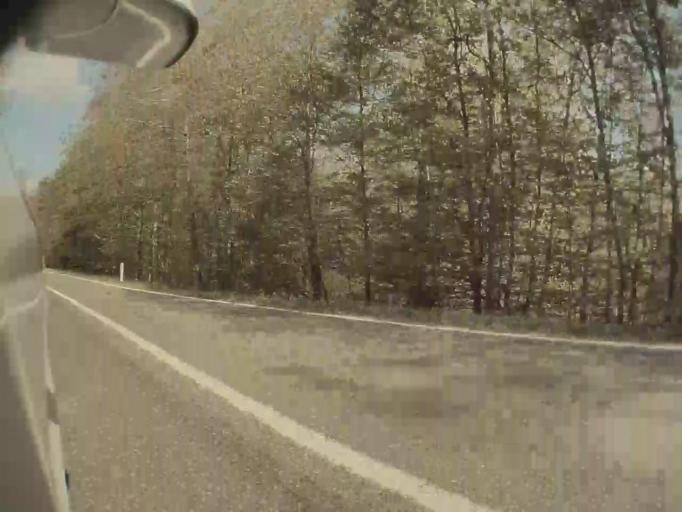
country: BE
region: Wallonia
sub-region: Province du Luxembourg
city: Tellin
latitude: 50.0196
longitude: 5.2048
